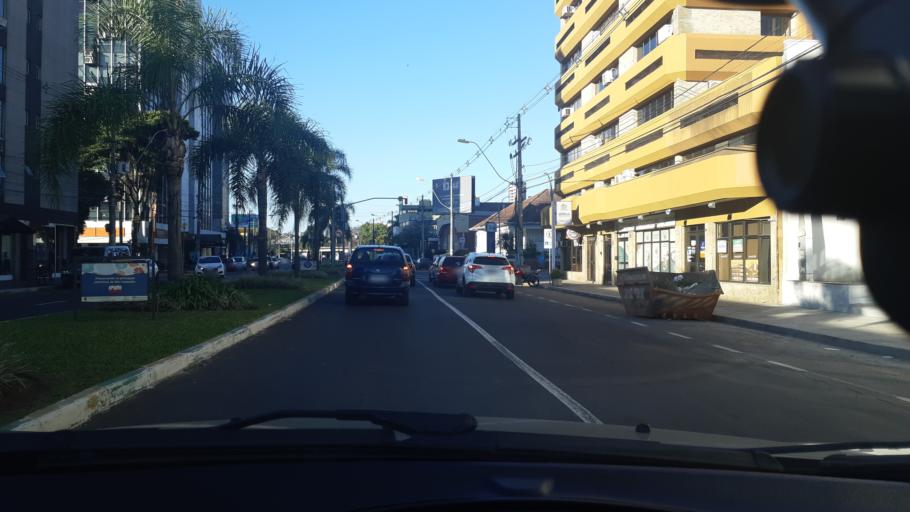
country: BR
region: Rio Grande do Sul
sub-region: Sao Leopoldo
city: Sao Leopoldo
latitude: -29.7711
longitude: -51.1452
